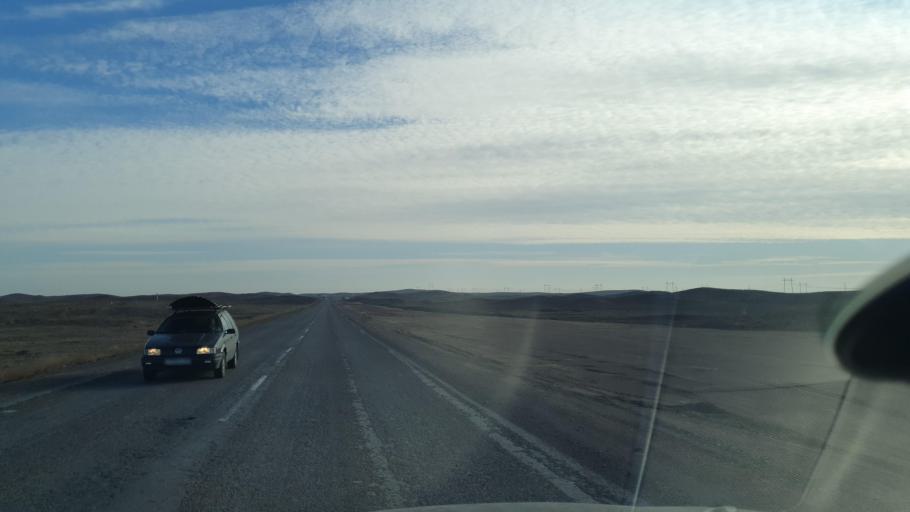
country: KZ
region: Zhambyl
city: Mynaral
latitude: 45.5329
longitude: 73.4771
